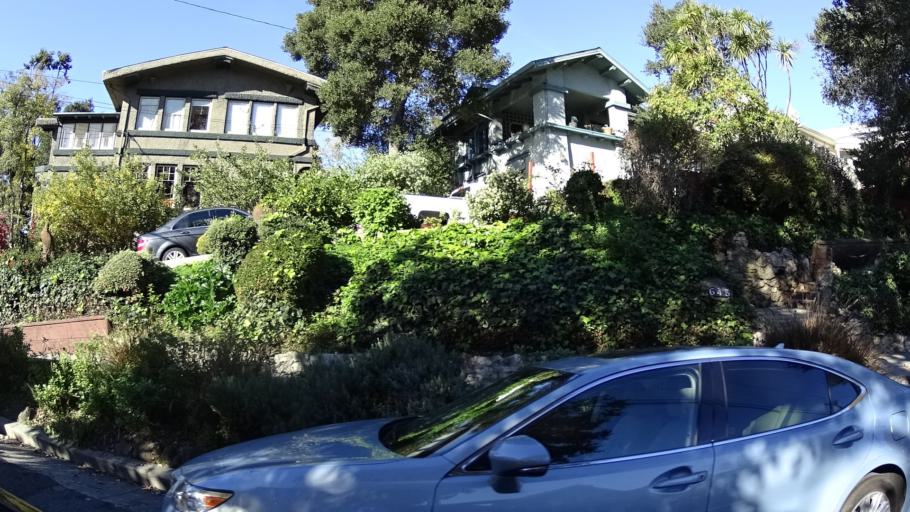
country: US
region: California
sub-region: Alameda County
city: Piedmont
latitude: 37.8114
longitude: -122.2396
